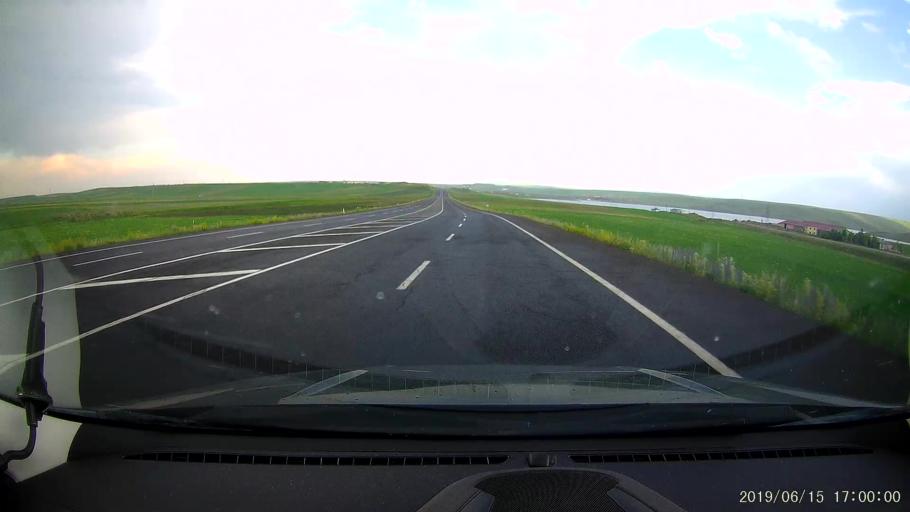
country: TR
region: Kars
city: Susuz
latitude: 40.7444
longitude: 43.1560
